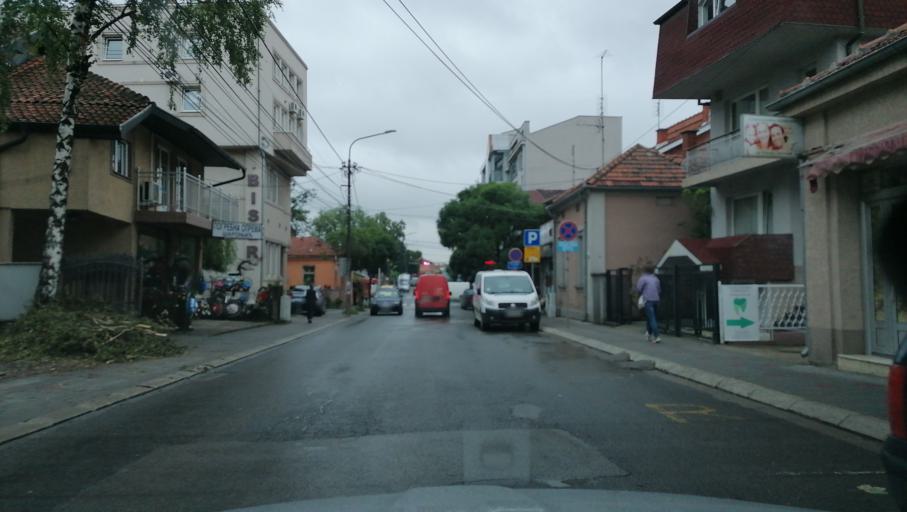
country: RS
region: Central Serbia
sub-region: Rasinski Okrug
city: Krusevac
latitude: 43.5808
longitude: 21.3222
